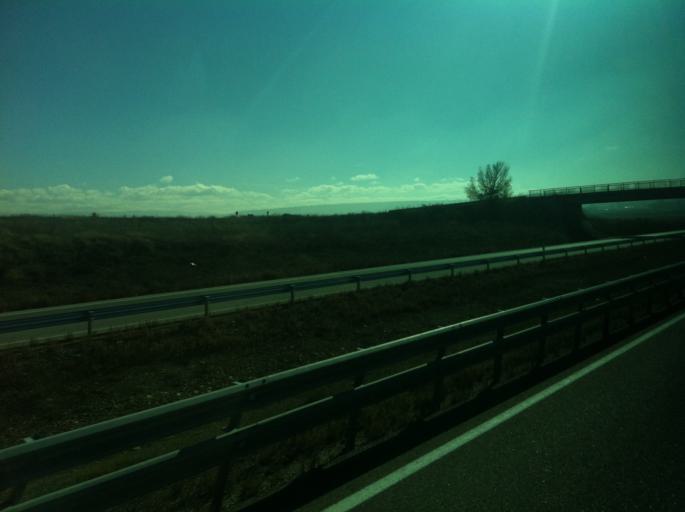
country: ES
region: Castille and Leon
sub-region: Provincia de Burgos
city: Cardenajimeno
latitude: 42.3511
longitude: -3.6032
